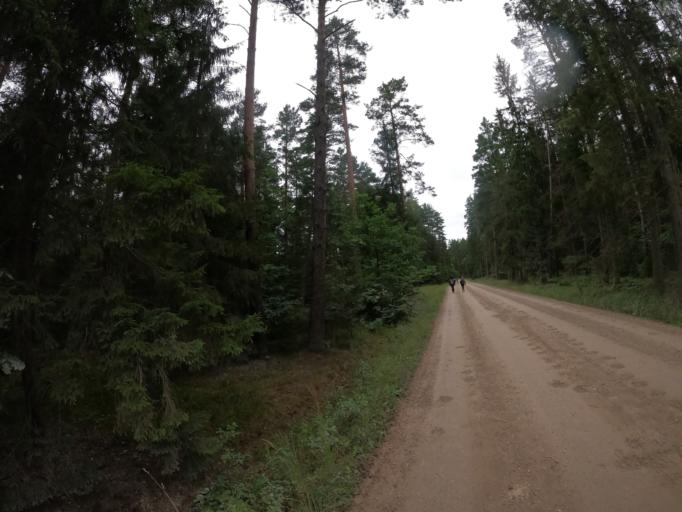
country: LV
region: Kuldigas Rajons
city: Kuldiga
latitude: 56.9986
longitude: 21.9795
